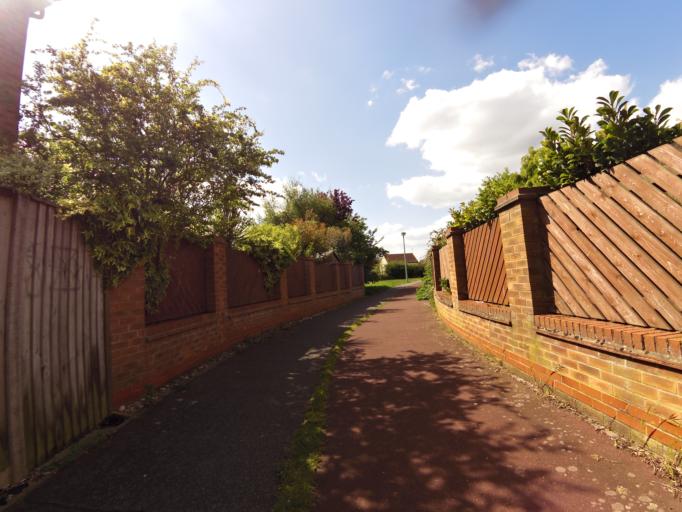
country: GB
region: England
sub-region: Suffolk
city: Kessingland
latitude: 52.4520
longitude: 1.7085
